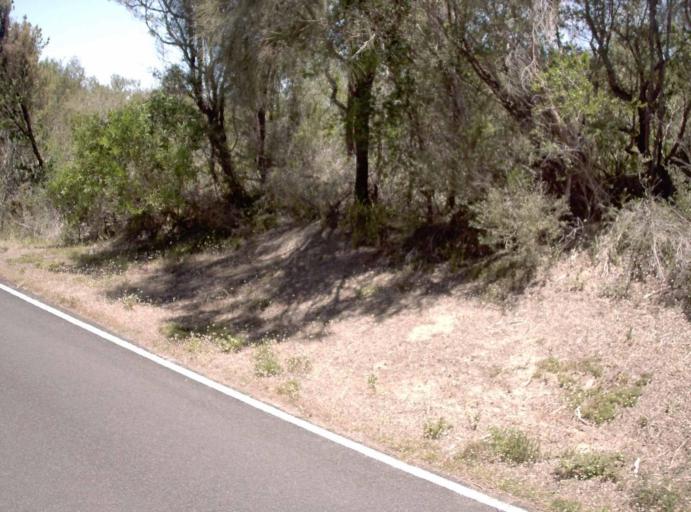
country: AU
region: Victoria
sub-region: Latrobe
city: Morwell
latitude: -38.8716
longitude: 146.2654
